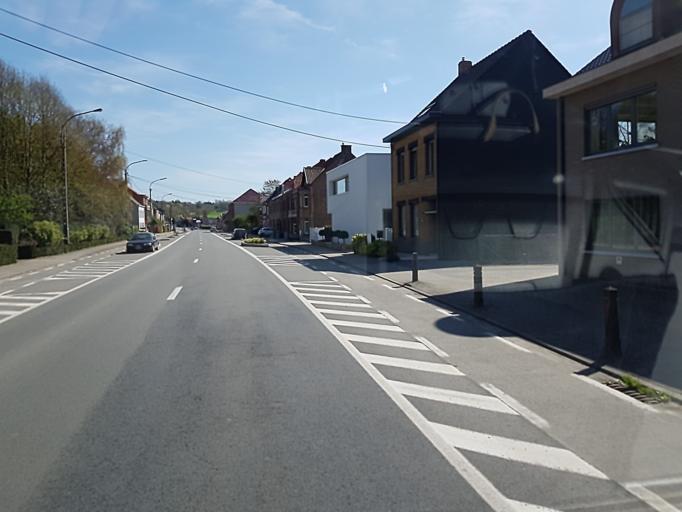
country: BE
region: Flanders
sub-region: Provincie West-Vlaanderen
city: Anzegem
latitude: 50.7870
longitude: 3.5121
